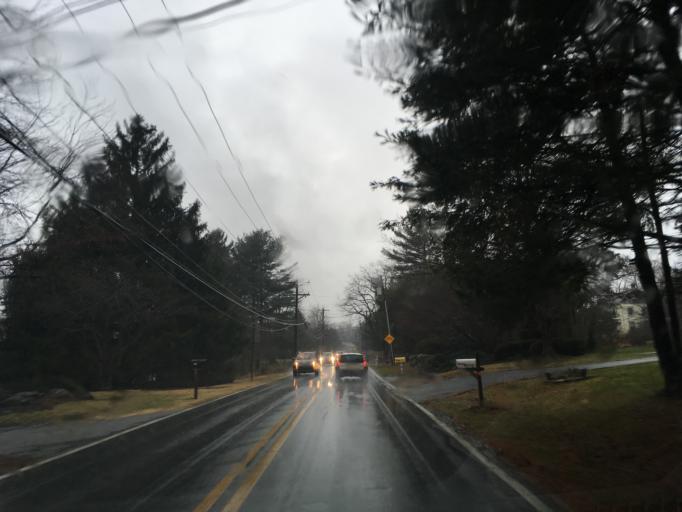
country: US
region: Delaware
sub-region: New Castle County
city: Bellefonte
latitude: 39.8213
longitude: -75.5204
